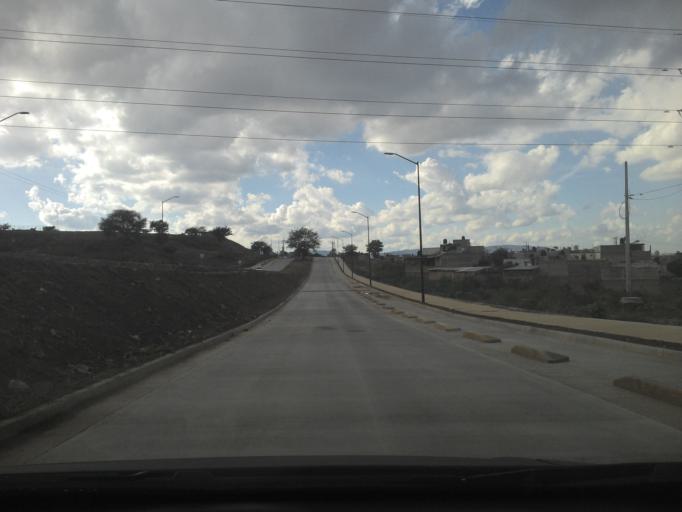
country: MX
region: Jalisco
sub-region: Tlajomulco de Zuniga
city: Altus Bosques
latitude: 20.6152
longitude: -103.3644
